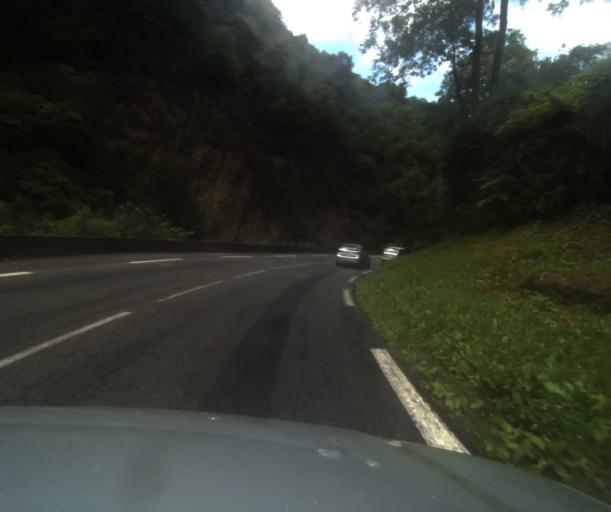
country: FR
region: Midi-Pyrenees
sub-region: Departement des Hautes-Pyrenees
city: Pierrefitte-Nestalas
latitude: 42.9399
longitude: -0.0530
